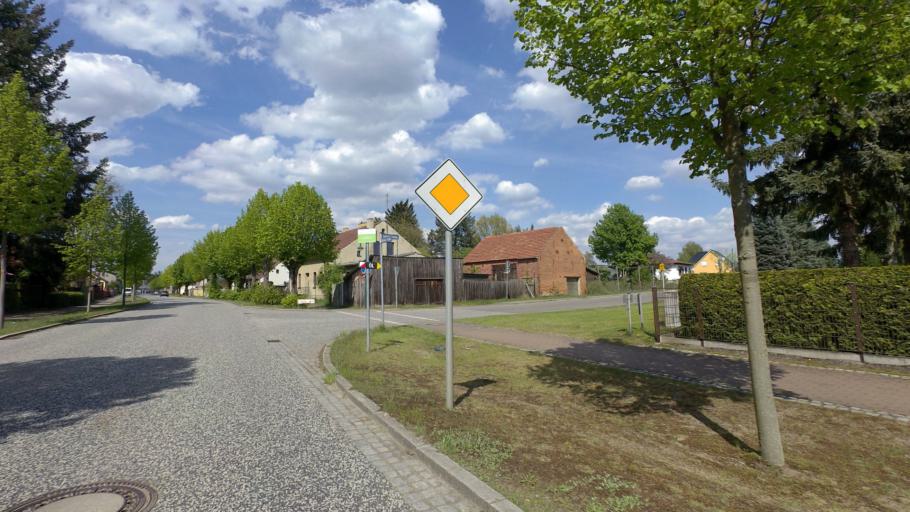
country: DE
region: Brandenburg
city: Marienwerder
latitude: 52.9014
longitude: 13.5358
